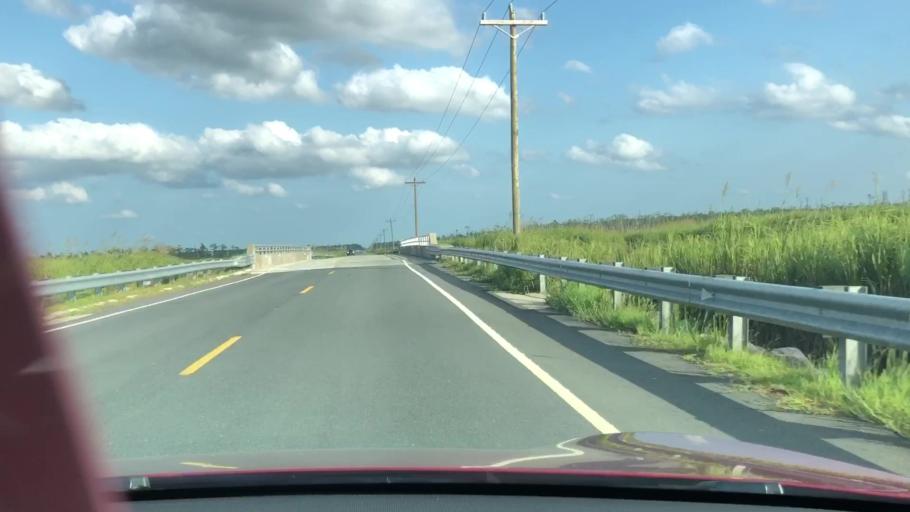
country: US
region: North Carolina
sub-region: Dare County
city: Wanchese
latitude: 35.6320
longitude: -75.8556
